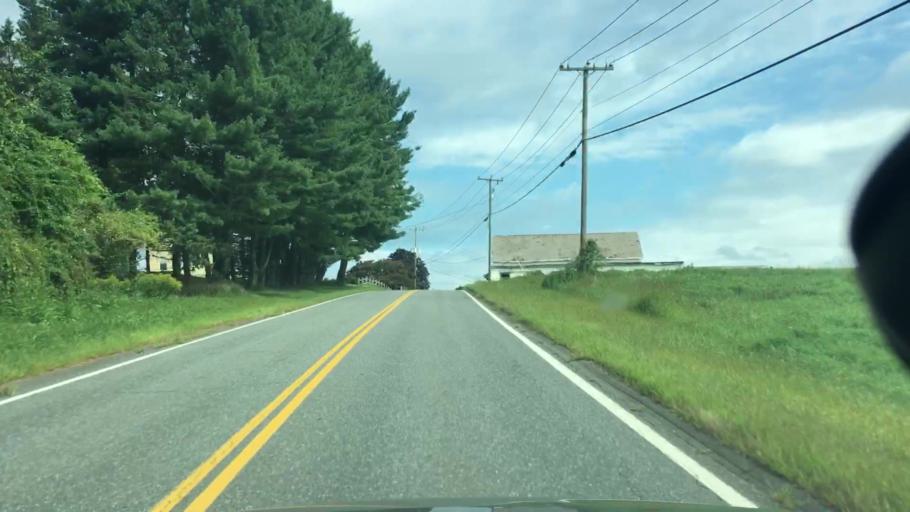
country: US
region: Massachusetts
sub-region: Franklin County
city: Shelburne
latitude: 42.6136
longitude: -72.6723
